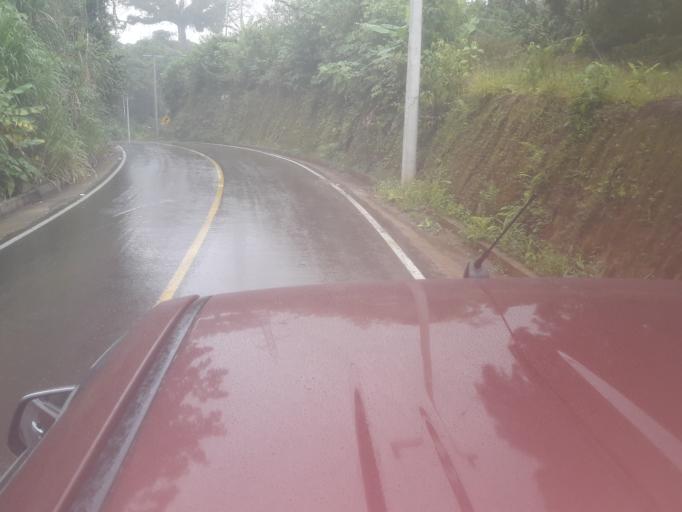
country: EC
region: Napo
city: Tena
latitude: -1.0240
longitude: -77.6677
